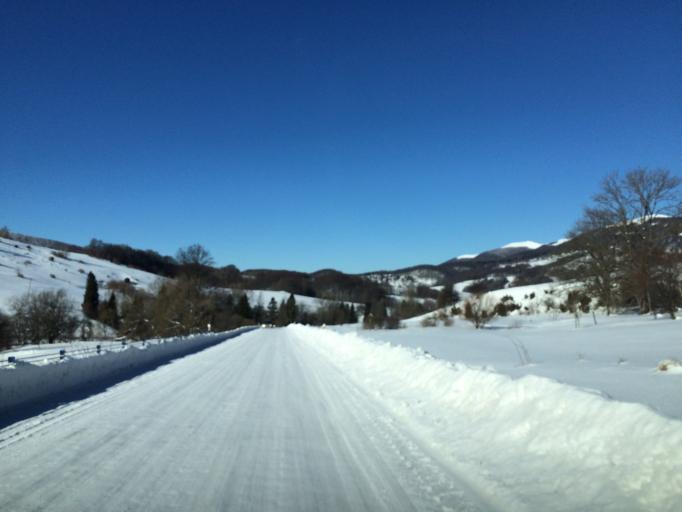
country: PL
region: Subcarpathian Voivodeship
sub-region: Powiat bieszczadzki
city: Lutowiska
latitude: 49.1293
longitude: 22.5831
